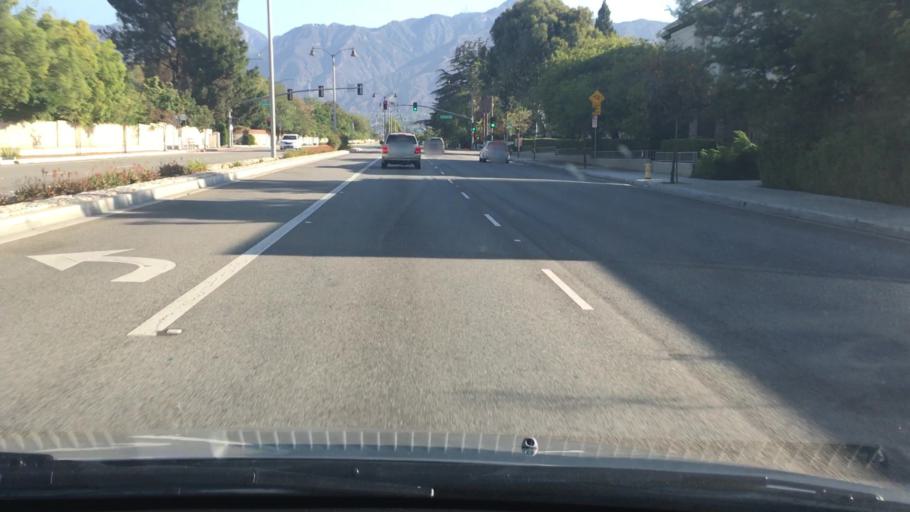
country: US
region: California
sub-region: Los Angeles County
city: East Pasadena
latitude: 34.1336
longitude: -118.0732
